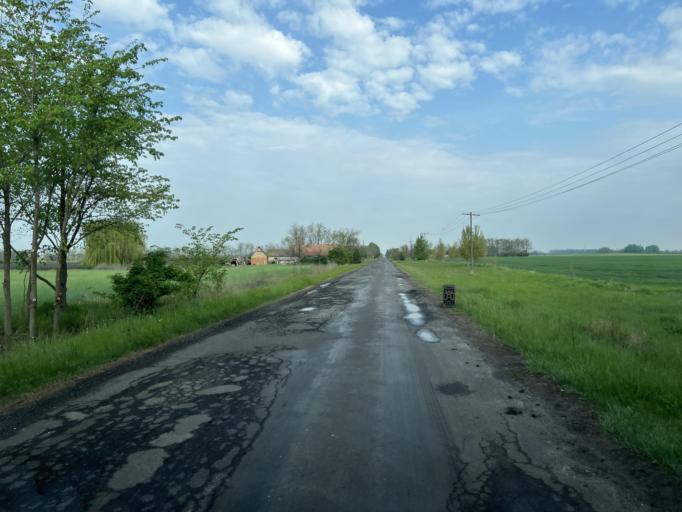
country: HU
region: Pest
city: Abony
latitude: 47.1577
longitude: 20.0502
